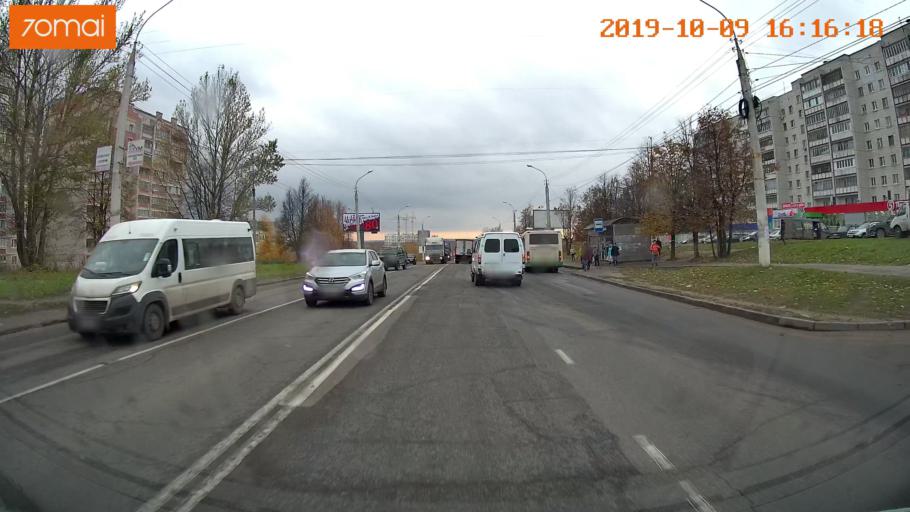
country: RU
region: Kostroma
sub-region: Kostromskoy Rayon
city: Kostroma
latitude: 57.7350
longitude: 40.9089
